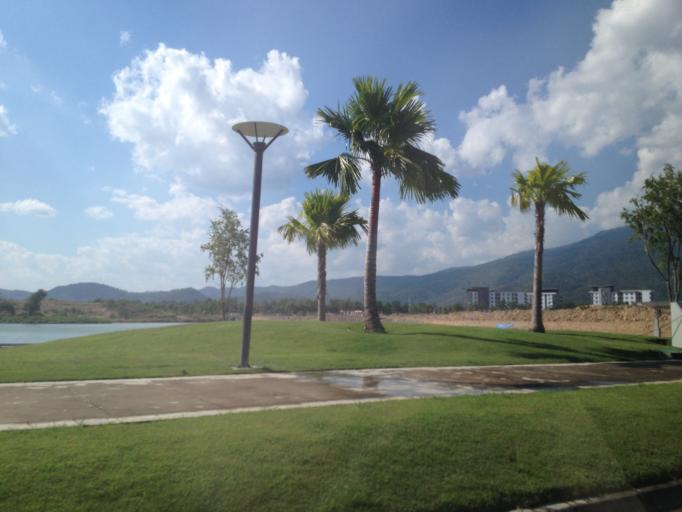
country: TH
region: Chiang Mai
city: Chiang Mai
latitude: 18.7569
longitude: 98.9546
